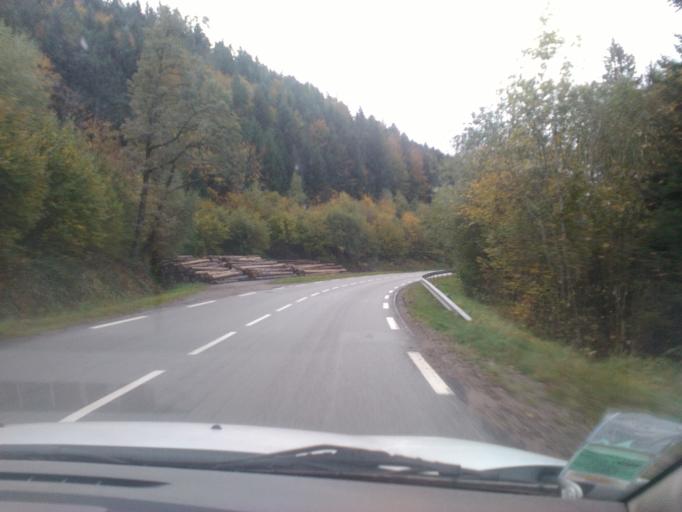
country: FR
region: Lorraine
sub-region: Departement des Vosges
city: Xonrupt-Longemer
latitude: 48.1308
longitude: 6.9165
